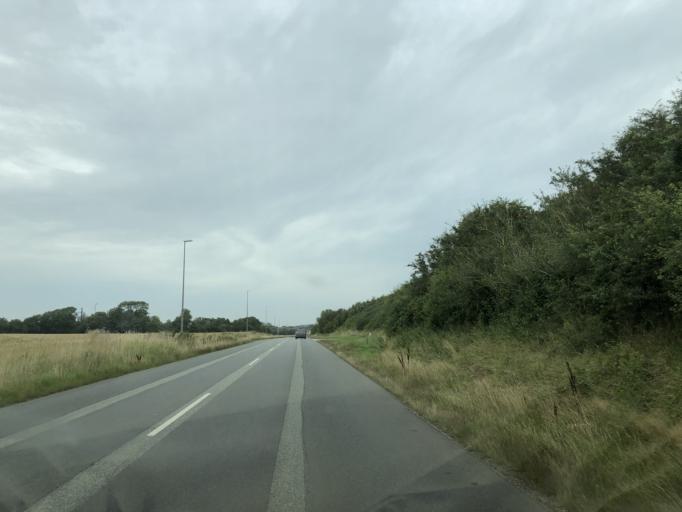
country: DK
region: North Denmark
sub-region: Morso Kommune
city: Nykobing Mors
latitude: 56.7956
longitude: 8.8356
